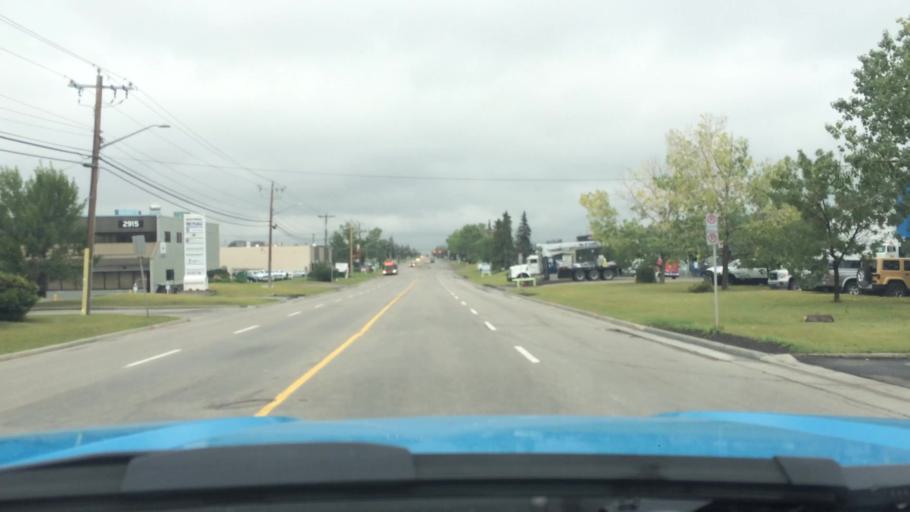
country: CA
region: Alberta
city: Calgary
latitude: 51.0775
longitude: -114.0117
